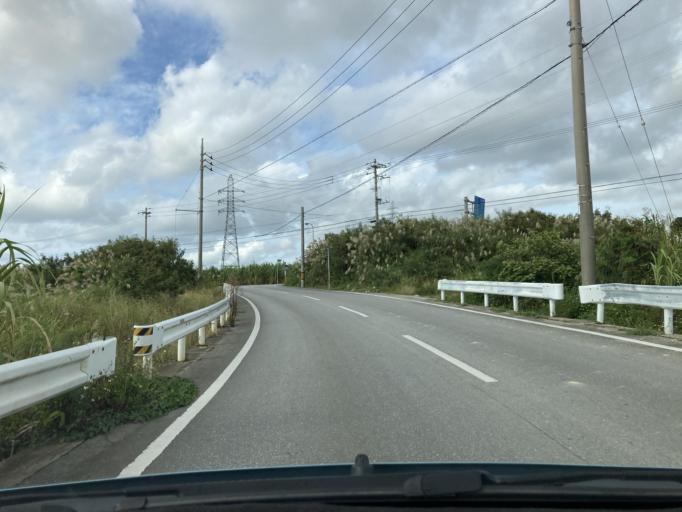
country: JP
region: Okinawa
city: Itoman
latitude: 26.1184
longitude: 127.6877
